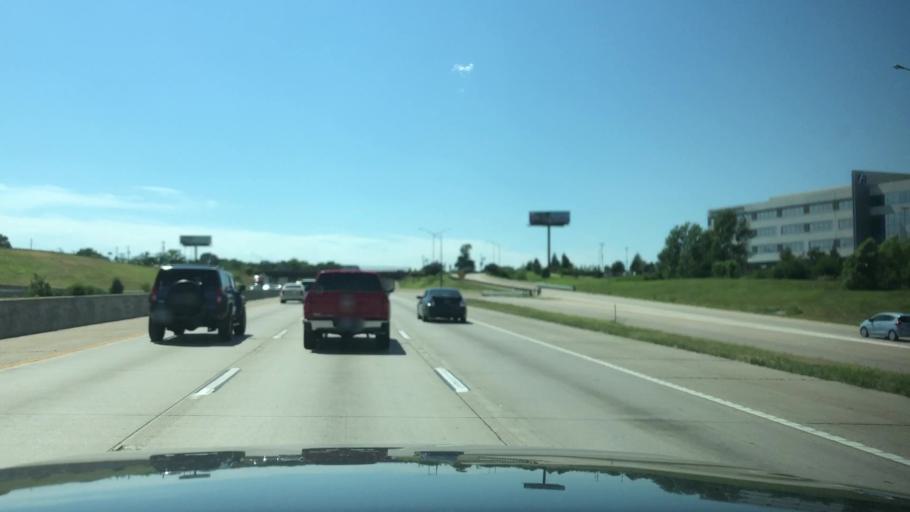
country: US
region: Missouri
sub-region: Saint Louis County
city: Cool Valley
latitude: 38.7208
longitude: -90.3132
